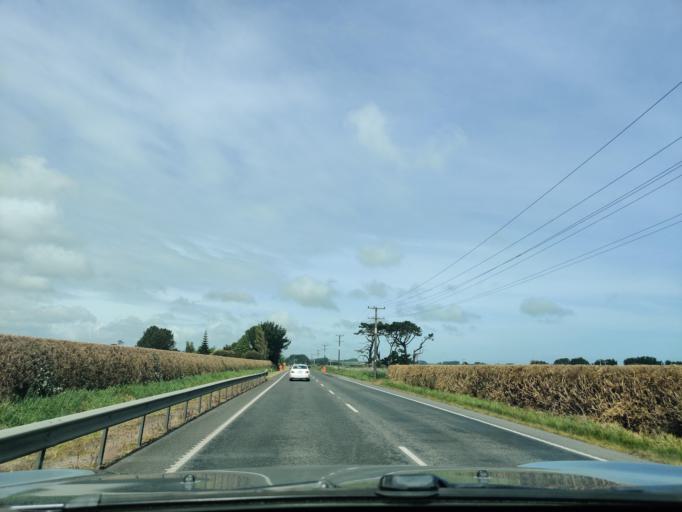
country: NZ
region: Taranaki
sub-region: South Taranaki District
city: Hawera
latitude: -39.6290
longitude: 174.3736
